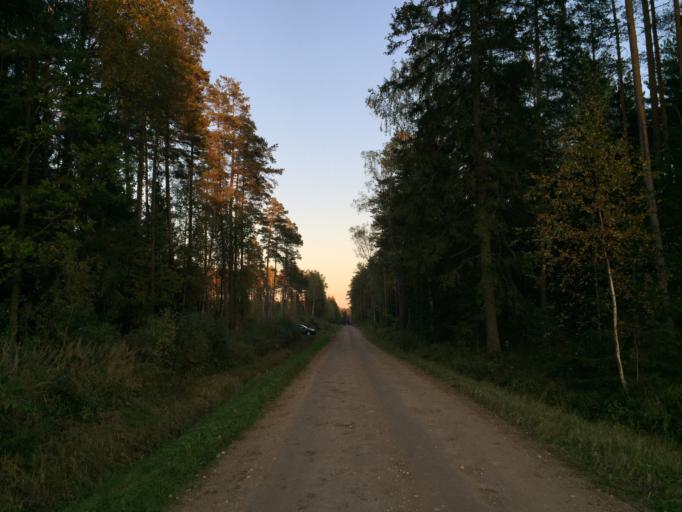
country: LV
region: Seja
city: Loja
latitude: 57.1282
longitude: 24.6159
